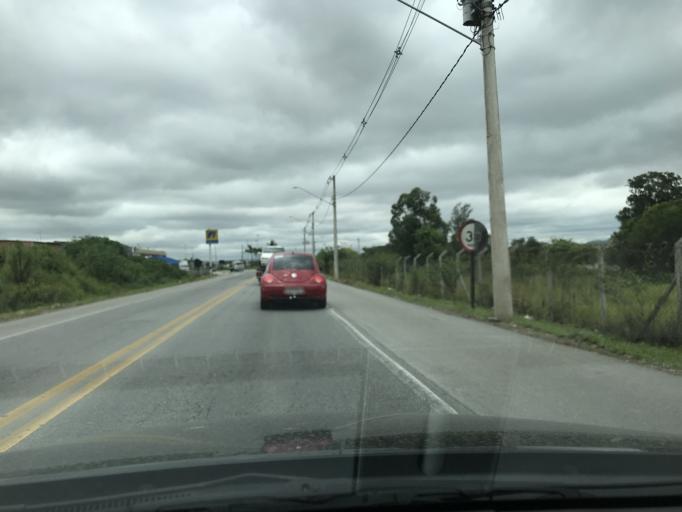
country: BR
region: Sao Paulo
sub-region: Itaquaquecetuba
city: Itaquaquecetuba
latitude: -23.4934
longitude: -46.3257
